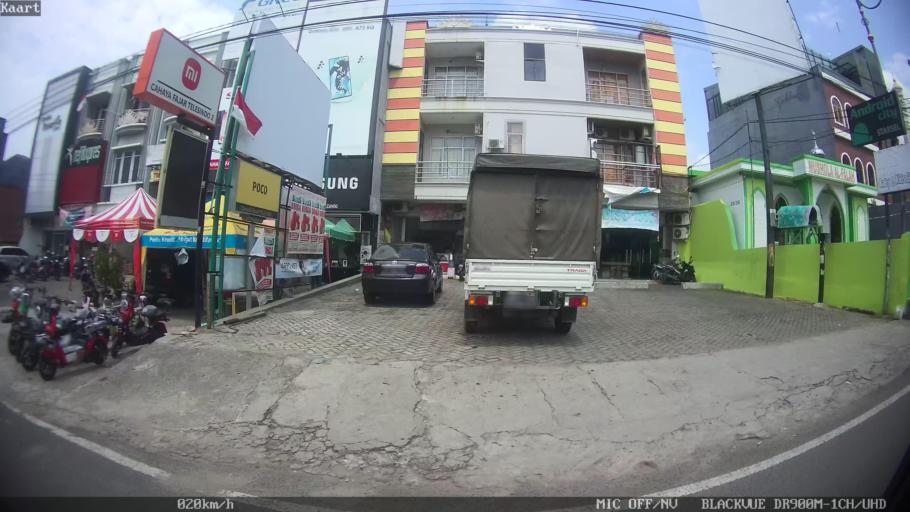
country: ID
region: Lampung
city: Bandarlampung
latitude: -5.4323
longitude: 105.2619
